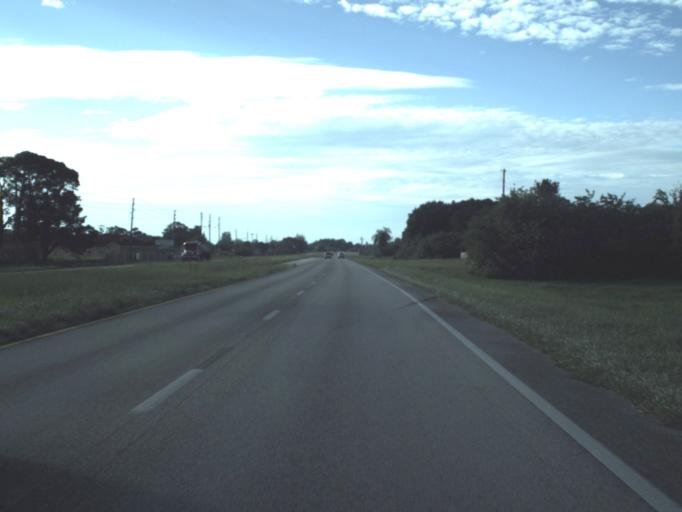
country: US
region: Florida
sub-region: Highlands County
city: Lake Placid
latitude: 27.2420
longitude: -81.3350
